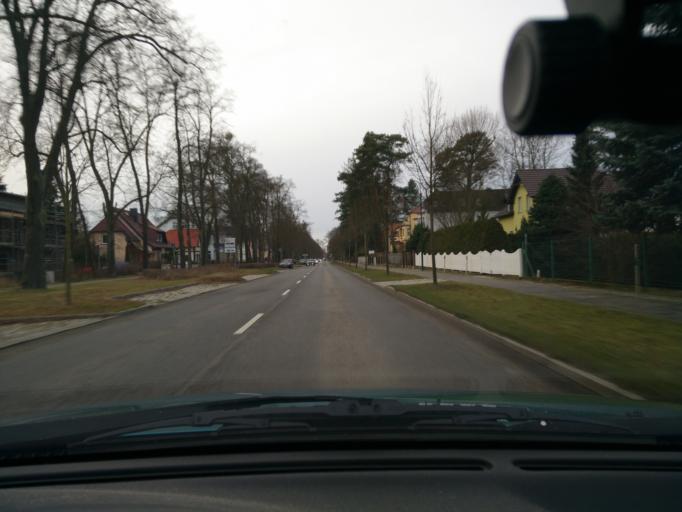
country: DE
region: Brandenburg
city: Biesenthal
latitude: 52.7581
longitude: 13.6646
